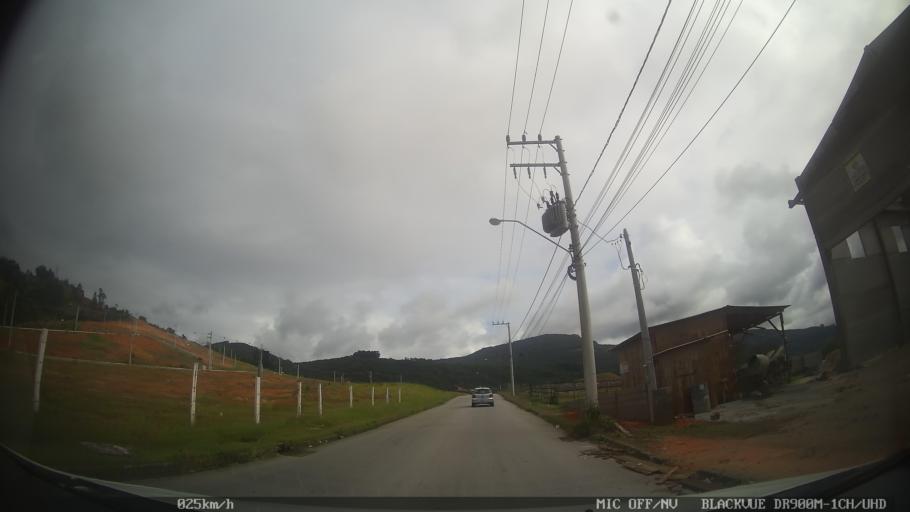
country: BR
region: Santa Catarina
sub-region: Biguacu
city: Biguacu
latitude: -27.5275
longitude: -48.6510
